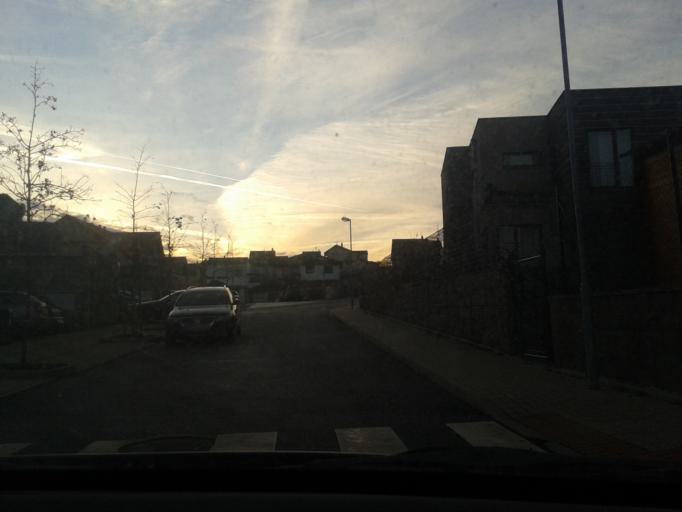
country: CZ
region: Central Bohemia
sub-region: Okres Beroun
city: Kraluv Dvur
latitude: 49.9332
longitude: 14.0138
